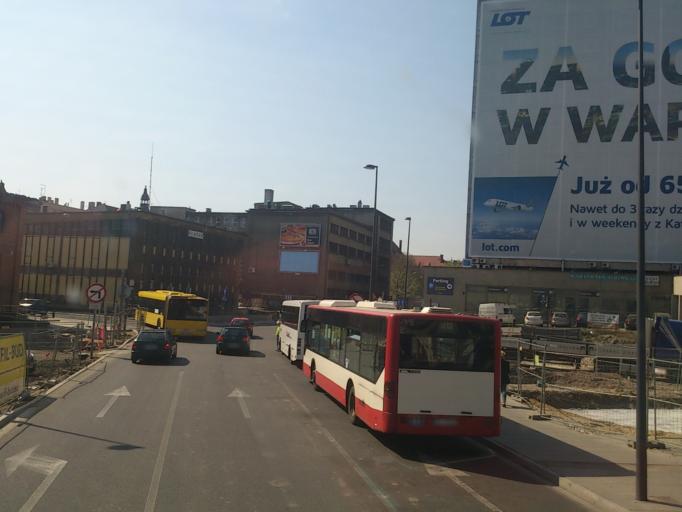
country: PL
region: Silesian Voivodeship
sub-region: Katowice
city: Katowice
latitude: 50.2610
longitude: 19.0215
